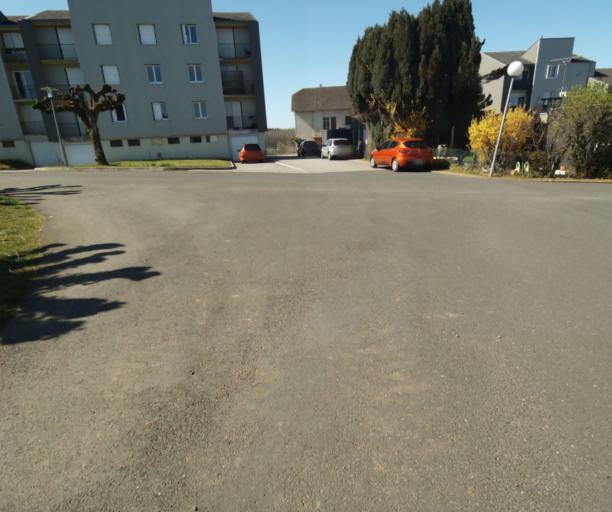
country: FR
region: Limousin
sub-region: Departement de la Correze
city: Seilhac
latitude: 45.3651
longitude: 1.7158
